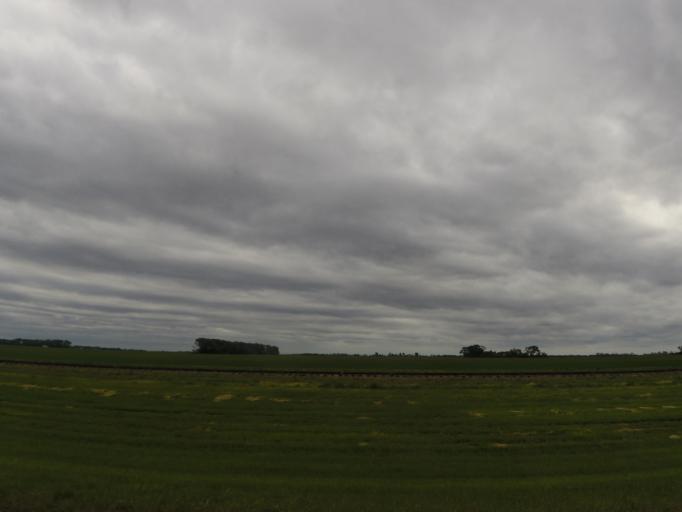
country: US
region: North Dakota
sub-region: Walsh County
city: Grafton
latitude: 48.5476
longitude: -97.4480
